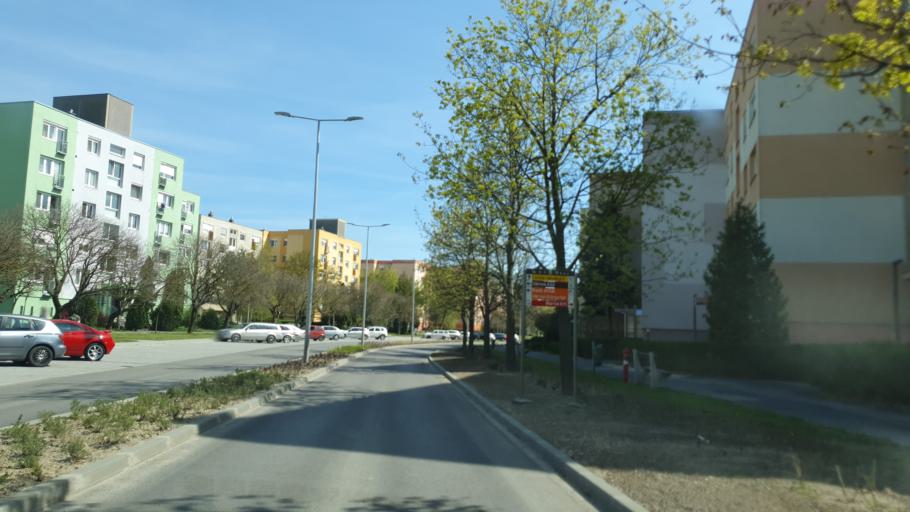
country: HU
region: Fejer
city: Mor
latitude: 47.3709
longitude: 18.2099
